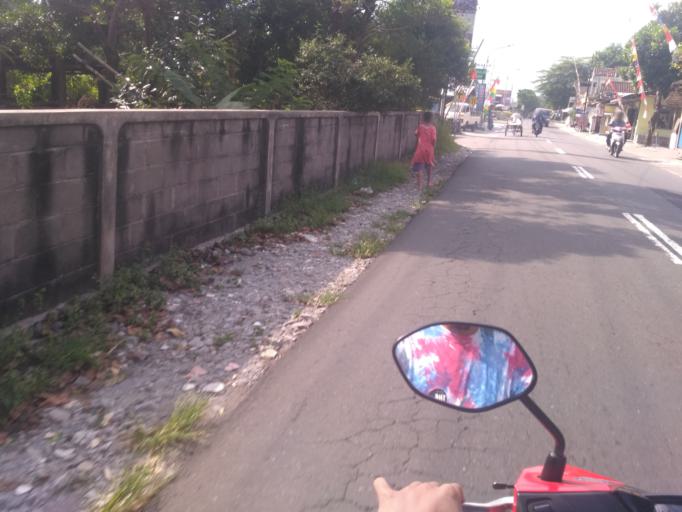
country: ID
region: Daerah Istimewa Yogyakarta
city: Godean
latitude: -7.7492
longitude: 110.3208
